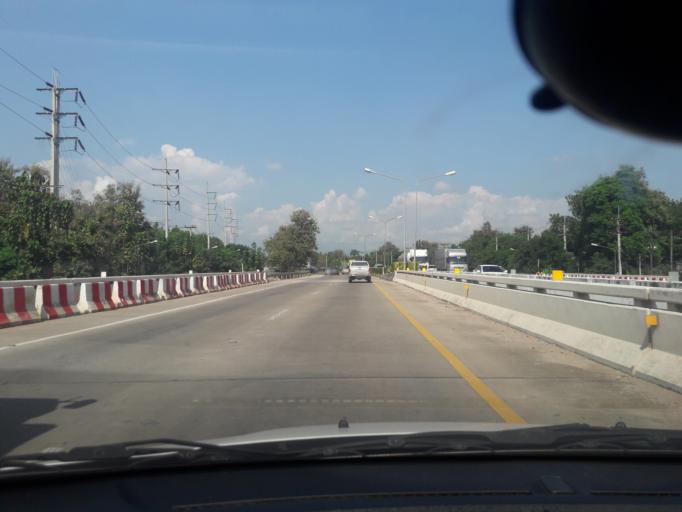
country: TH
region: Lampang
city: Lampang
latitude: 18.2700
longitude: 99.4635
